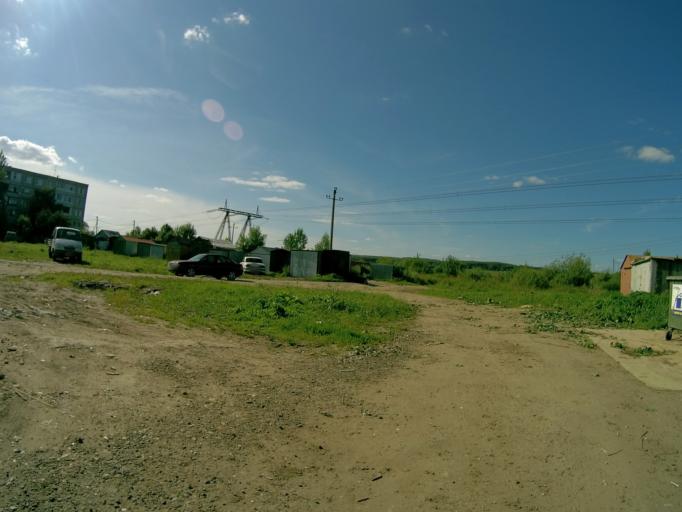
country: RU
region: Vladimir
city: Vorsha
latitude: 56.0994
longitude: 40.2008
